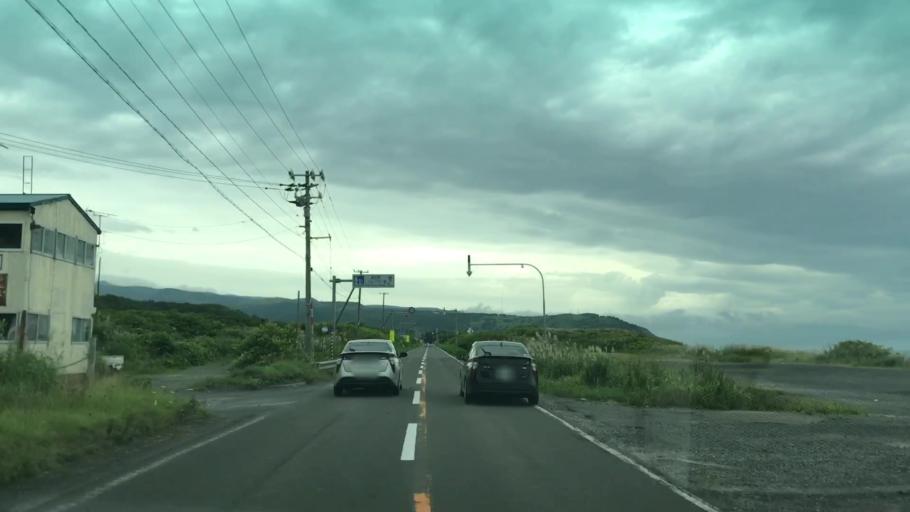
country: JP
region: Hokkaido
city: Iwanai
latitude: 42.8955
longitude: 140.3775
